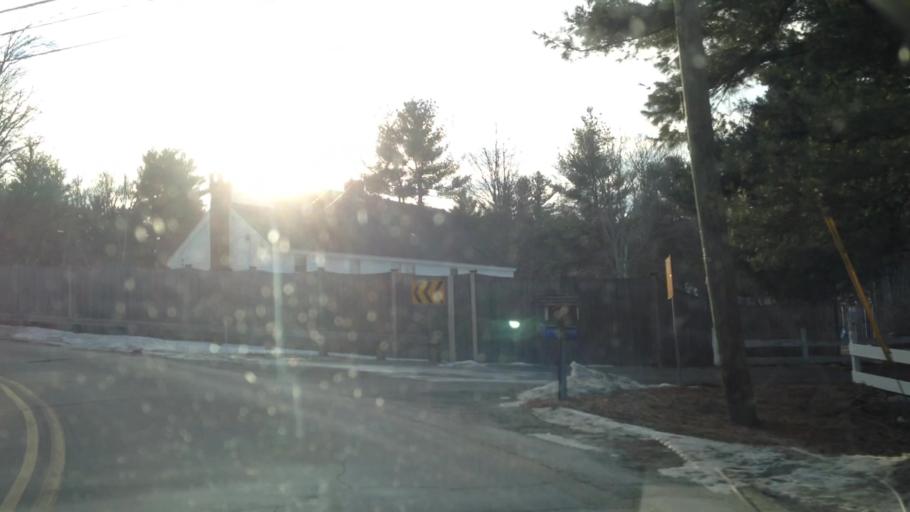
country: US
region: New Hampshire
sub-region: Hillsborough County
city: Merrimack
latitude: 42.8330
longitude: -71.5639
